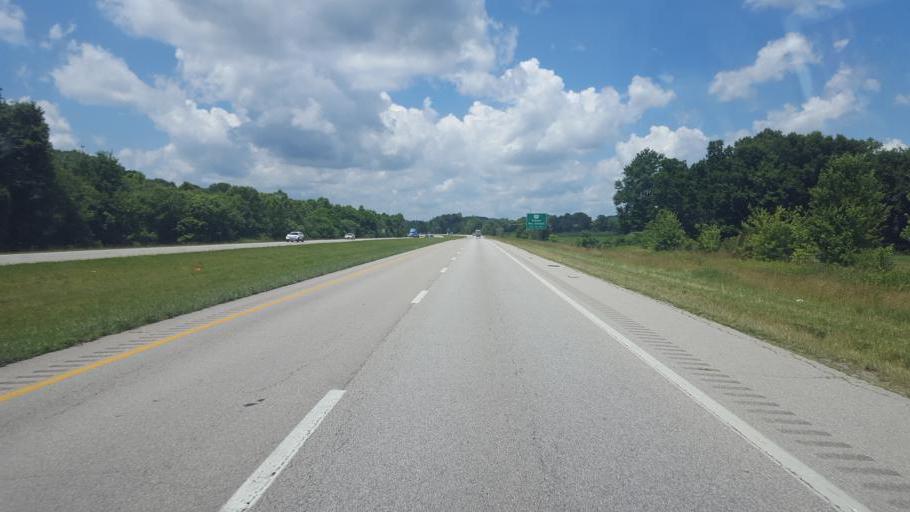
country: US
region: Ohio
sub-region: Gallia County
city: Gallipolis
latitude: 38.8939
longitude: -82.3687
